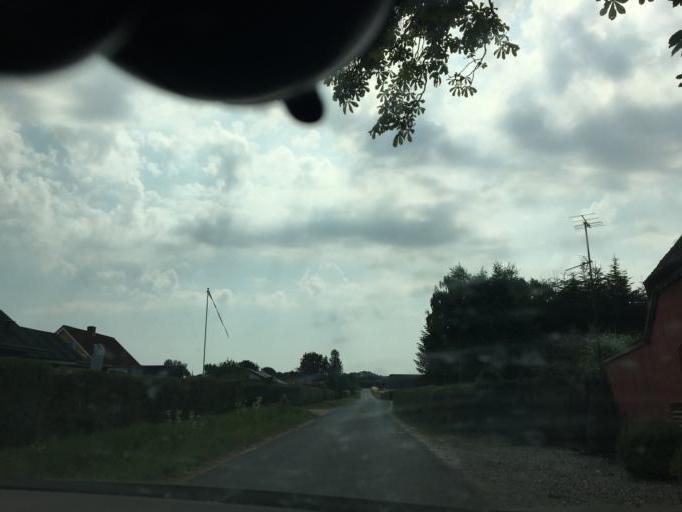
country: DK
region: South Denmark
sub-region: Middelfart Kommune
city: Norre Aby
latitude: 55.5097
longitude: 9.8837
